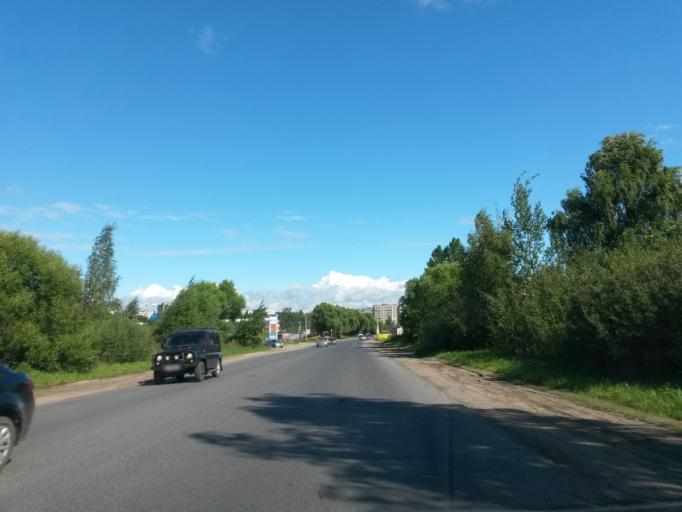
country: RU
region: Jaroslavl
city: Yaroslavl
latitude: 57.5650
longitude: 39.8579
